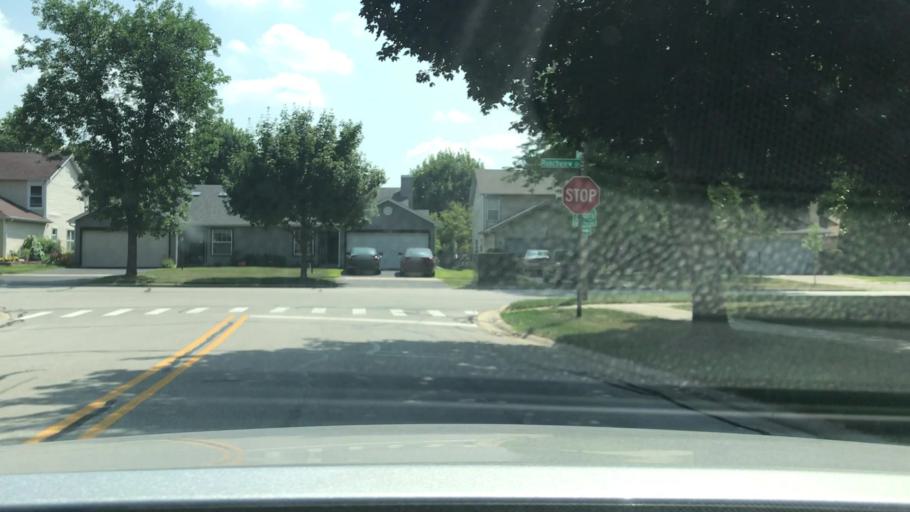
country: US
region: Illinois
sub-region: DuPage County
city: Woodridge
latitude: 41.7429
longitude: -88.0965
